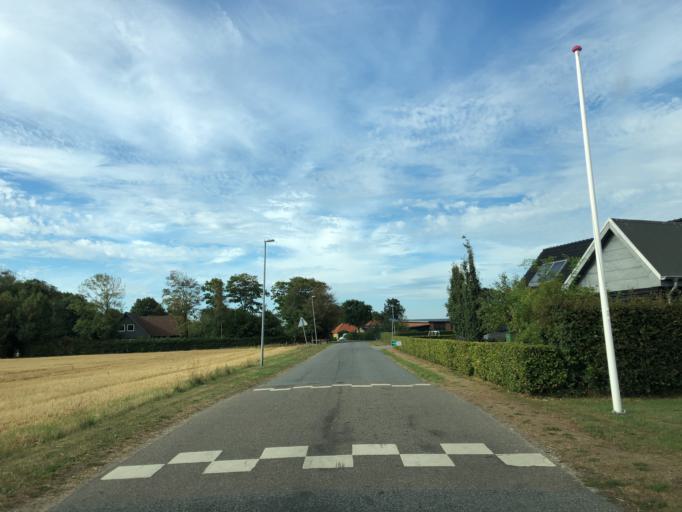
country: DK
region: Central Jutland
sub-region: Ringkobing-Skjern Kommune
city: Skjern
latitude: 56.0554
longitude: 8.4066
